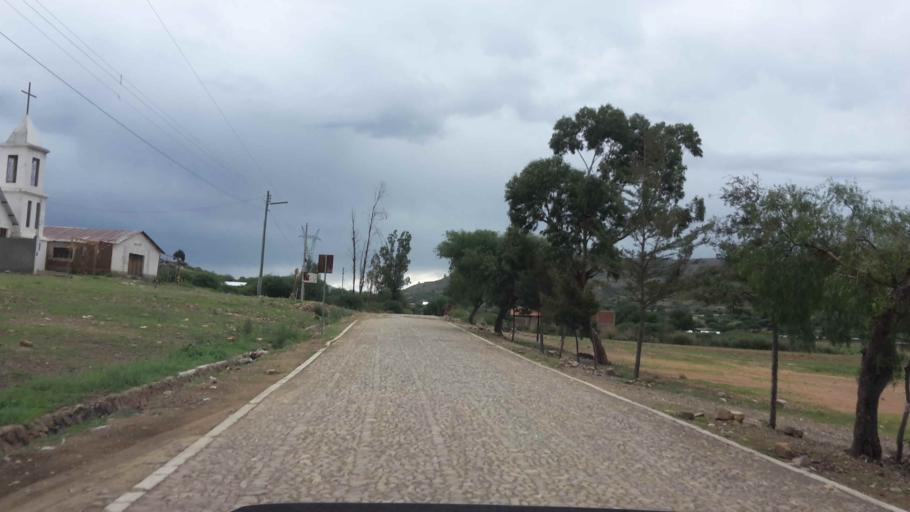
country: BO
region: Cochabamba
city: Cochabamba
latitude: -17.5450
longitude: -66.1891
